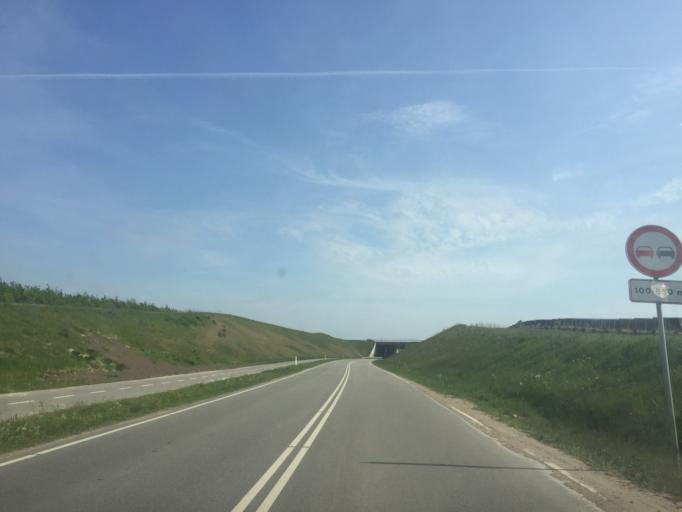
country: DK
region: Capital Region
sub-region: Egedal Kommune
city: Smorumnedre
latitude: 55.7209
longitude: 12.2937
